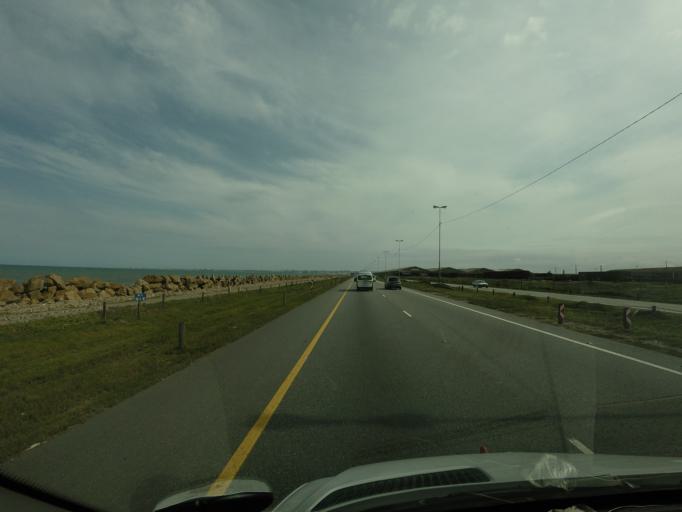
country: ZA
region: Eastern Cape
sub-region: Nelson Mandela Bay Metropolitan Municipality
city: Port Elizabeth
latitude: -33.8988
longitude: 25.6200
